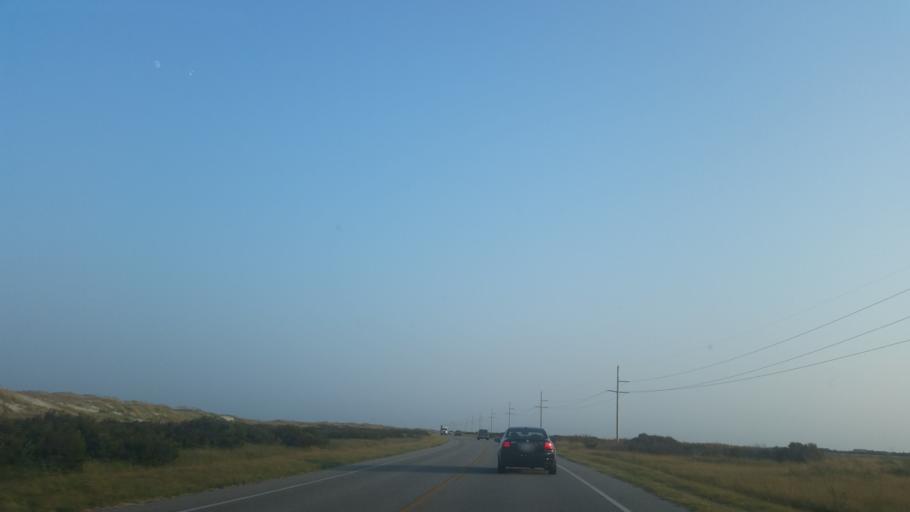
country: US
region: North Carolina
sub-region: Dare County
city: Wanchese
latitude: 35.7119
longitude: -75.4922
